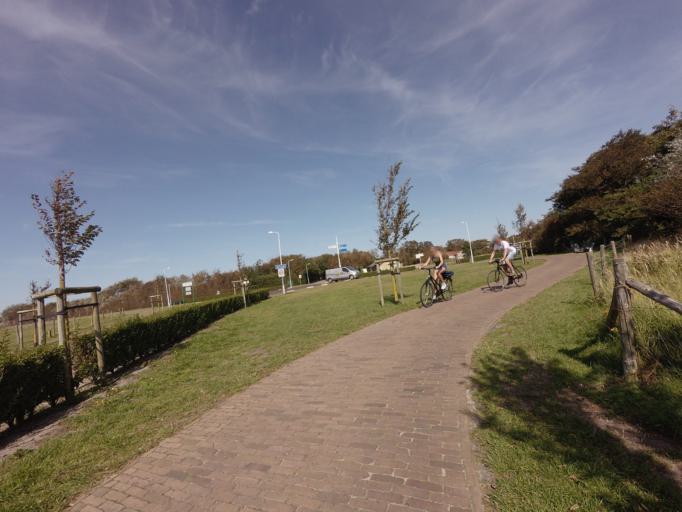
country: NL
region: Friesland
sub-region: Gemeente Ameland
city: Hollum
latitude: 53.4454
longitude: 5.6351
